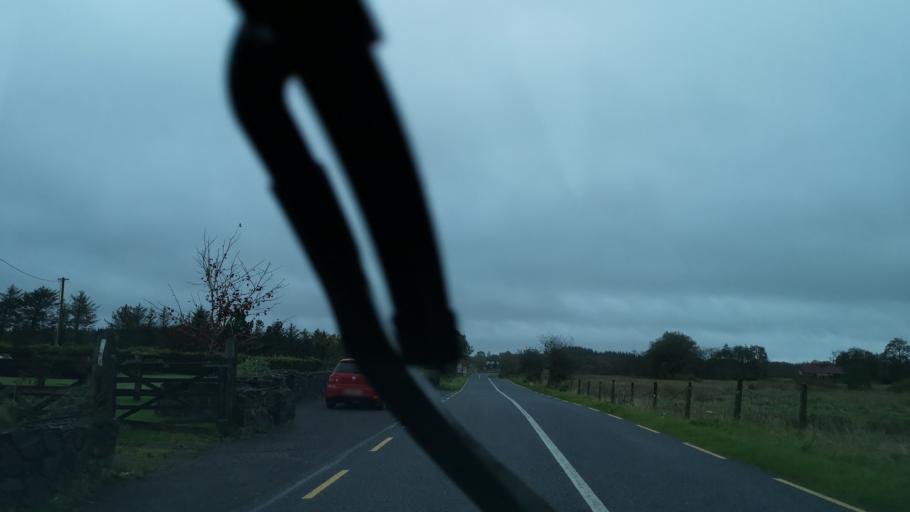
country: IE
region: Connaught
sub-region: Maigh Eo
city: Ballyhaunis
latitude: 53.7994
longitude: -8.6990
